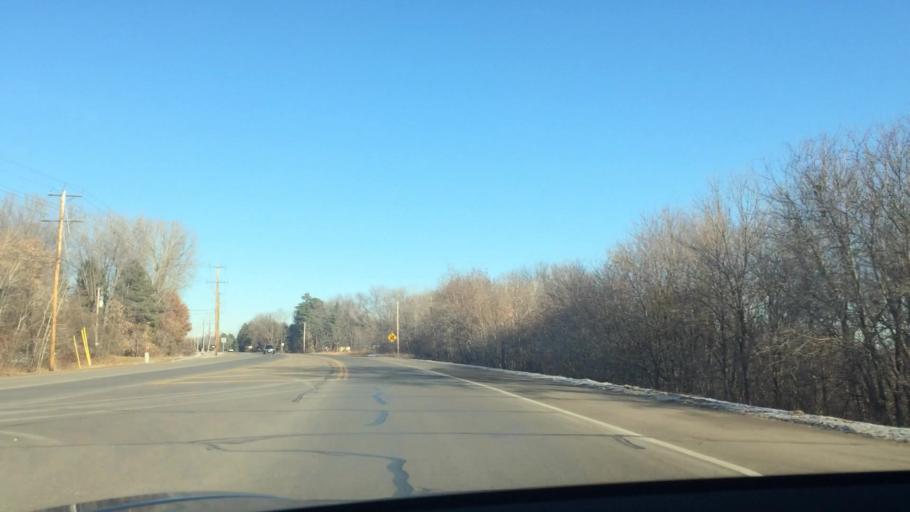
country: US
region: Minnesota
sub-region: Anoka County
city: Circle Pines
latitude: 45.1551
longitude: -93.1320
